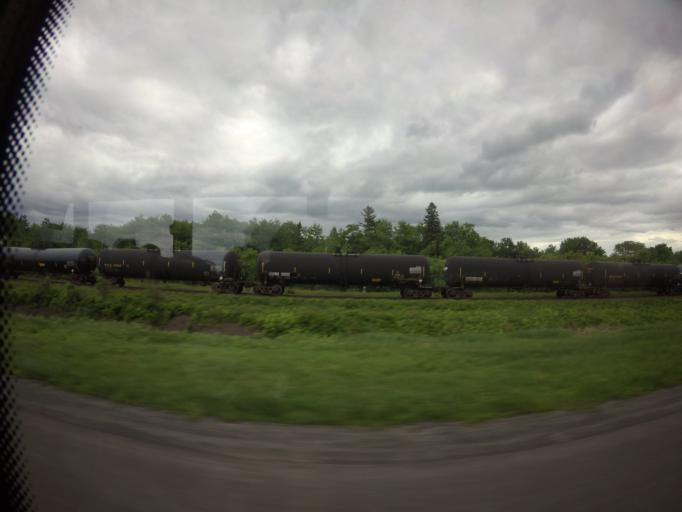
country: CA
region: Quebec
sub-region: Chaudiere-Appalaches
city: Saint-Antoine-de-Tilly
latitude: 46.5926
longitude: -71.5443
